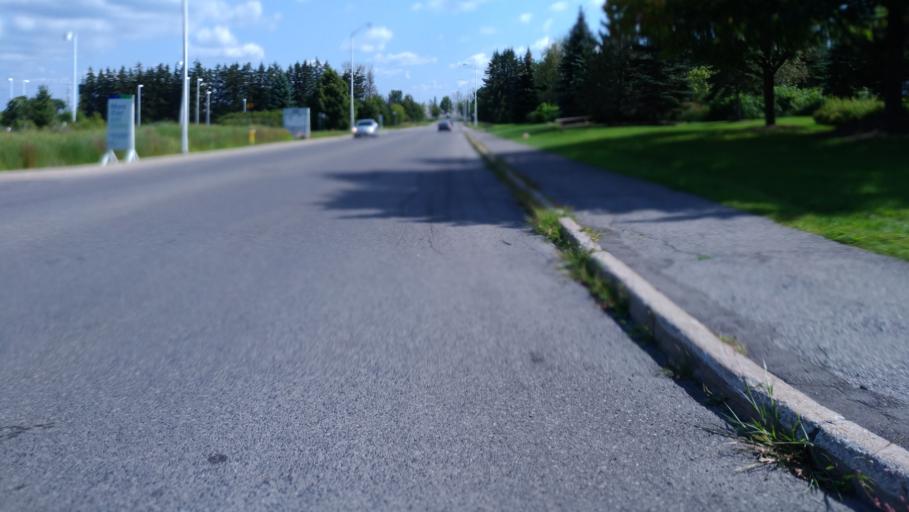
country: CA
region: Ontario
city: Bells Corners
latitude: 45.3442
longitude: -75.9225
